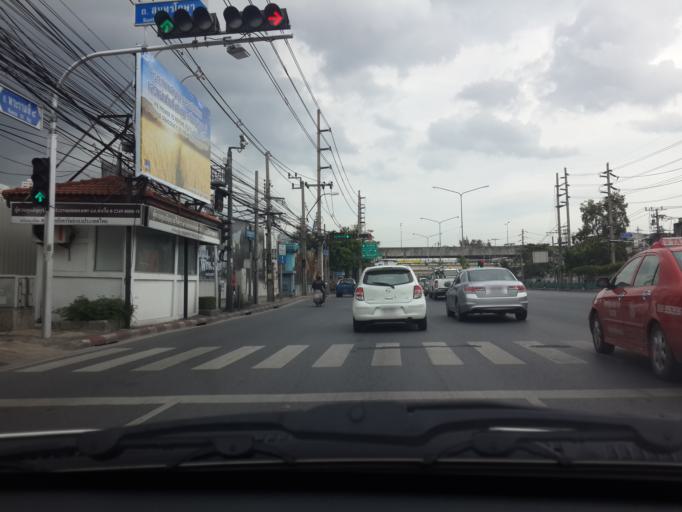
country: TH
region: Bangkok
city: Khlong Toei
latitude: 13.7210
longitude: 100.5573
